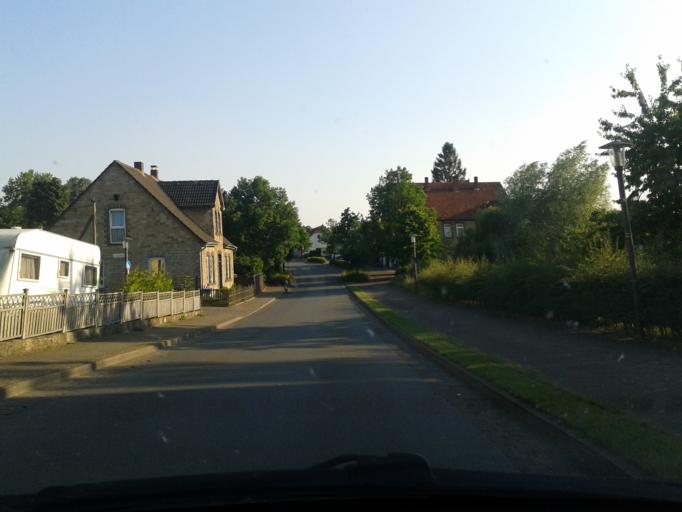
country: DE
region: North Rhine-Westphalia
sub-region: Regierungsbezirk Detmold
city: Lemgo
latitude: 51.9914
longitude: 8.9143
